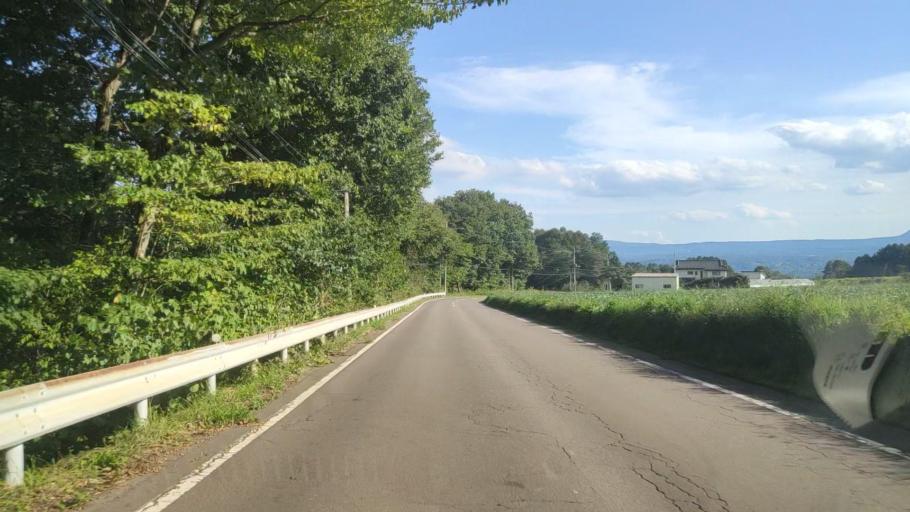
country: JP
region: Nagano
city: Suzaka
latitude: 36.5629
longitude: 138.5562
